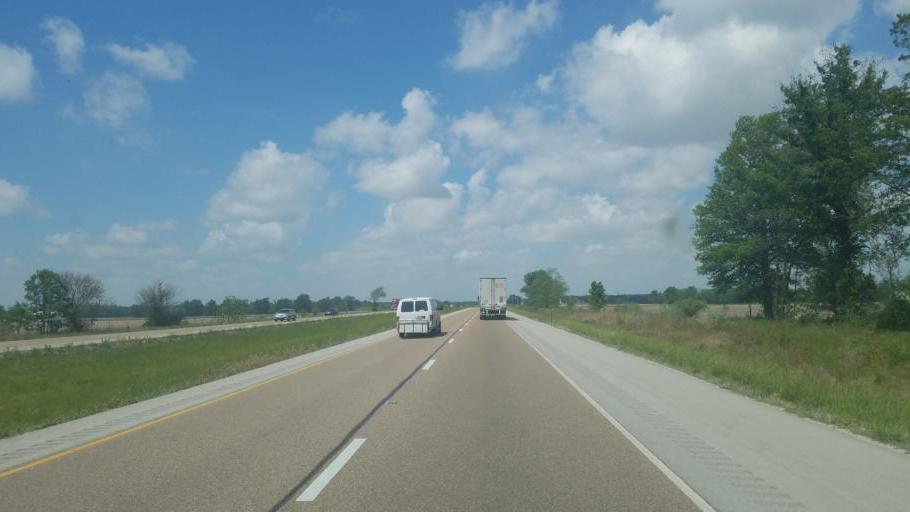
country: US
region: Illinois
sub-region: Cumberland County
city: Greenup
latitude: 39.2748
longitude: -88.0954
